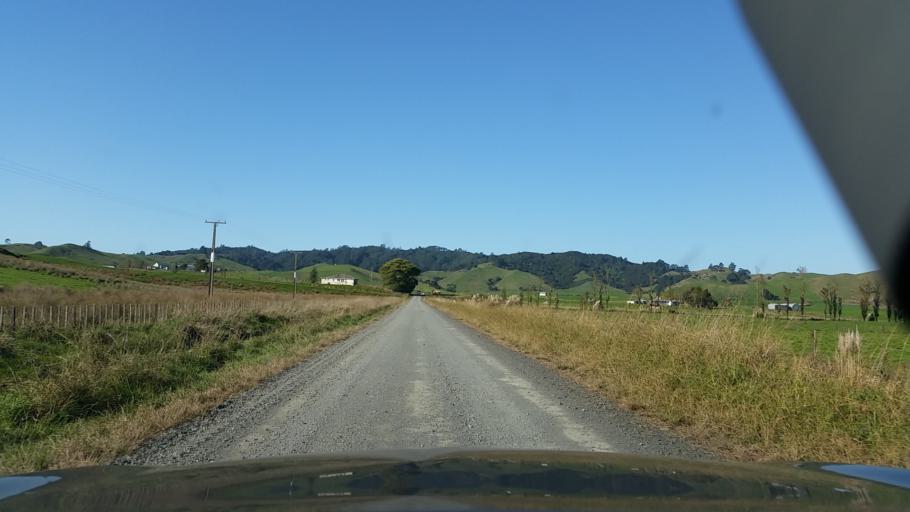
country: NZ
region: Waikato
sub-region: Hamilton City
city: Hamilton
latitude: -37.5707
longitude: 175.4161
